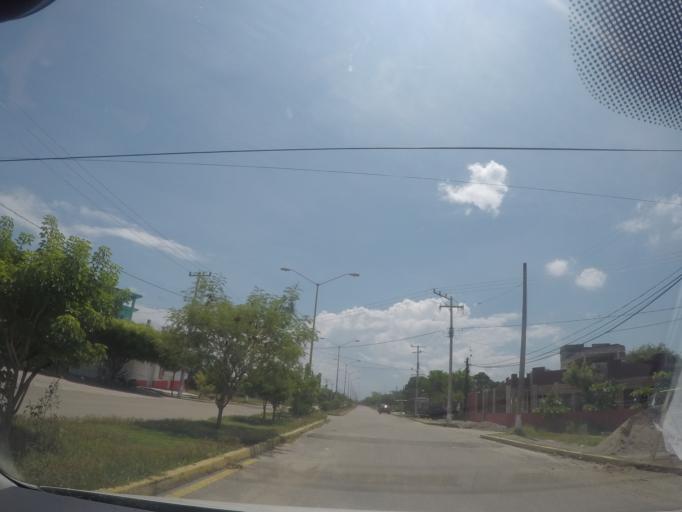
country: MX
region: Oaxaca
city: San Francisco Ixhuatan
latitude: 16.3992
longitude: -94.4578
